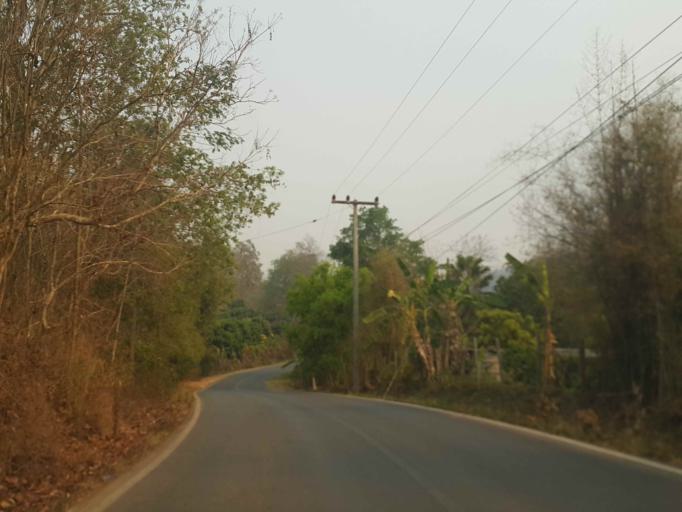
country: TH
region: Chiang Mai
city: Mae Taeng
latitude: 19.1271
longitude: 98.8843
